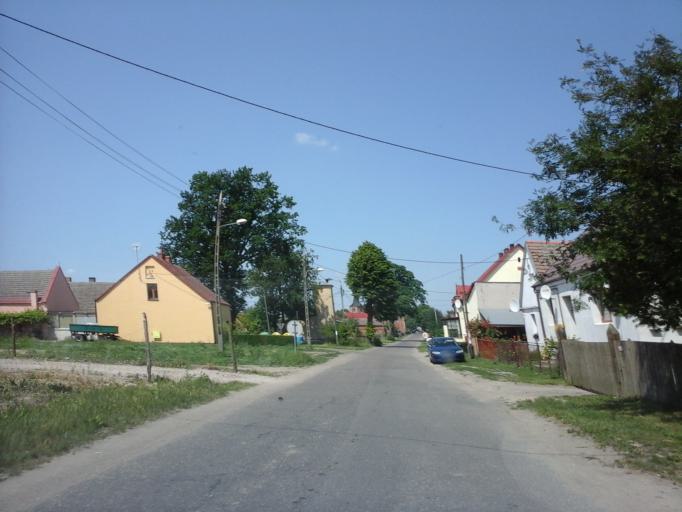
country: PL
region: West Pomeranian Voivodeship
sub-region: Powiat choszczenski
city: Choszczno
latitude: 53.1289
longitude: 15.3810
